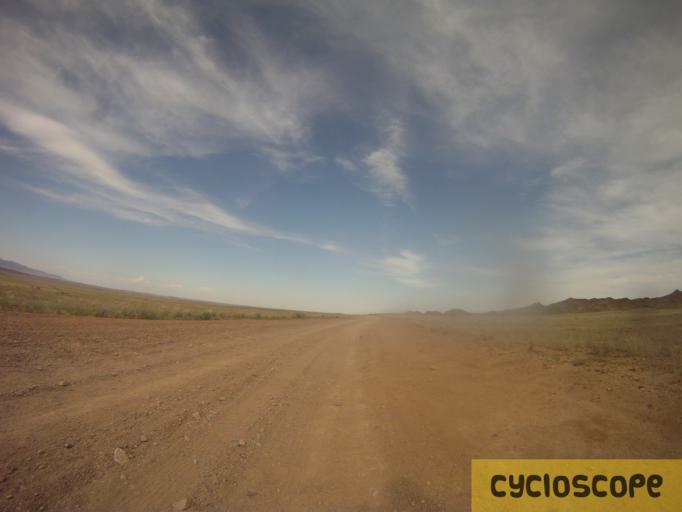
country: KZ
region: Almaty Oblysy
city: Kegen
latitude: 43.3579
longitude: 78.9848
